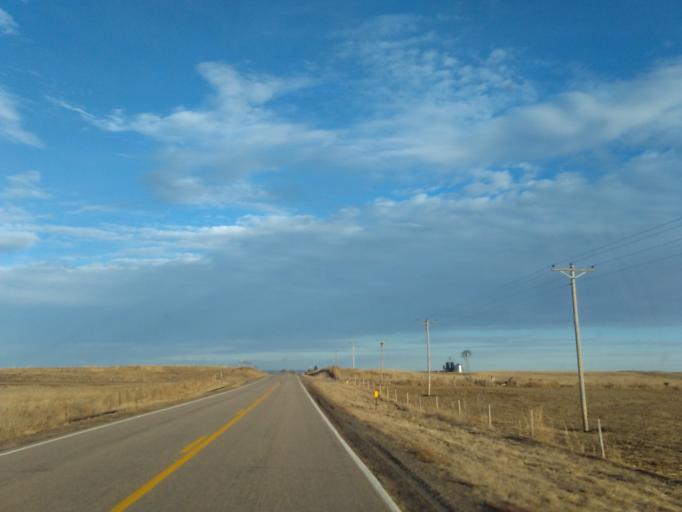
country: US
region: Nebraska
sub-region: Morrill County
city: Bridgeport
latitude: 41.5982
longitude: -102.9660
